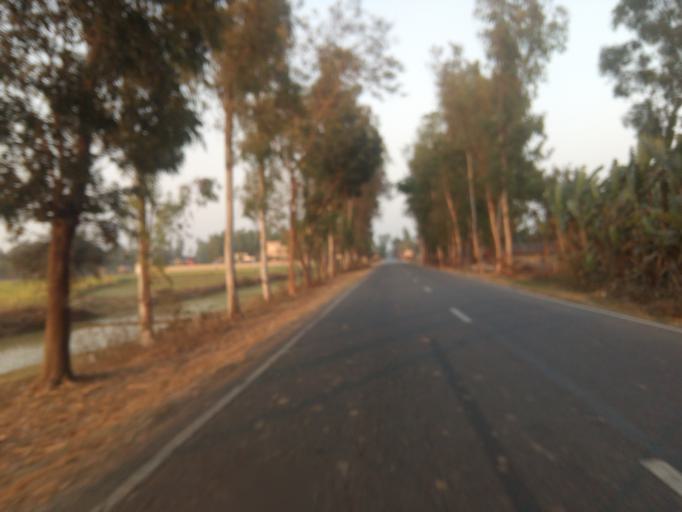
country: BD
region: Rajshahi
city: Bogra
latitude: 24.6359
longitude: 89.2490
